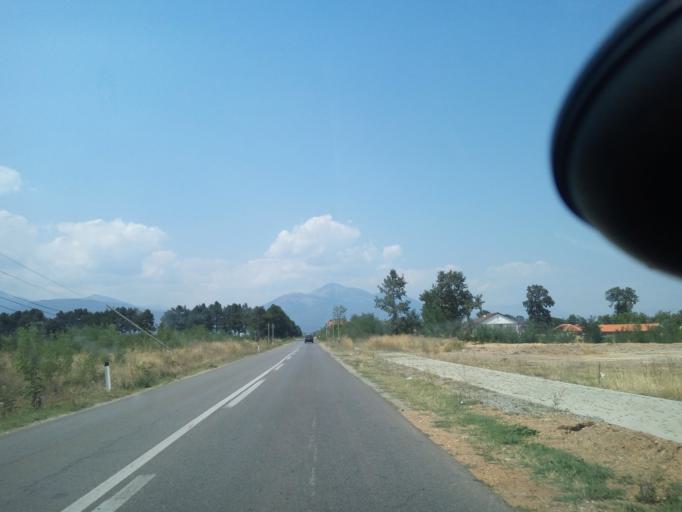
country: XK
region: Gjakova
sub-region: Komuna e Decanit
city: Gllogjan
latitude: 42.4698
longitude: 20.3441
